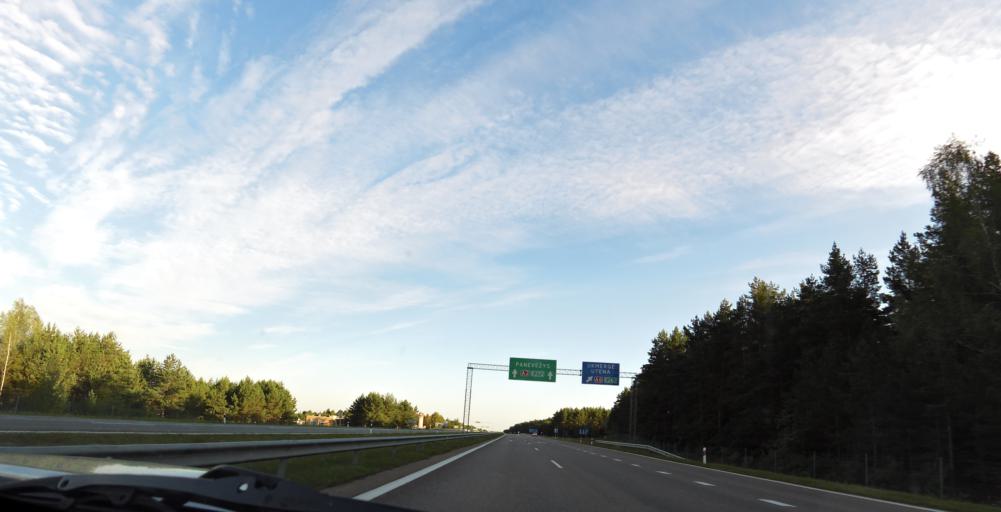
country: LT
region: Vilnius County
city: Ukmerge
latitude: 55.2671
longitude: 24.8123
